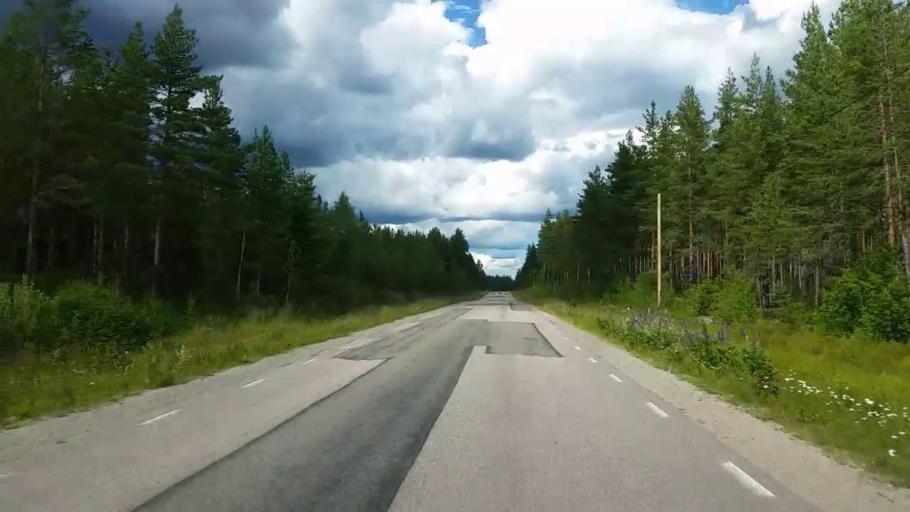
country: SE
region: Gaevleborg
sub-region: Ovanakers Kommun
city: Edsbyn
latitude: 61.4036
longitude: 15.8963
